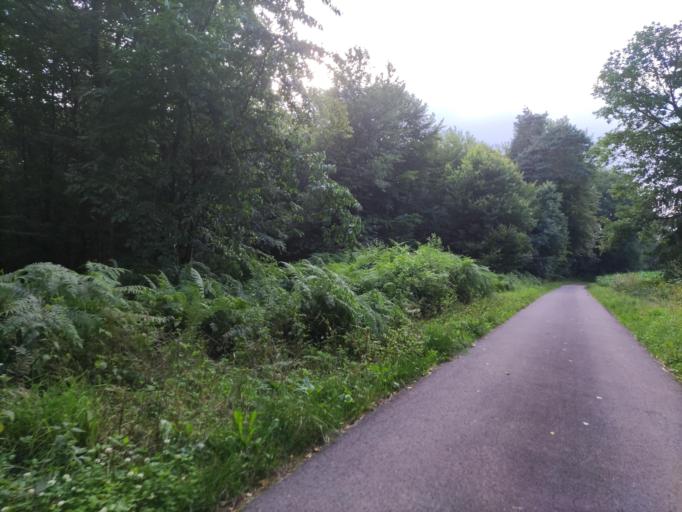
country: DE
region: Saarland
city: Nalbach
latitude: 49.4448
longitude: 6.7799
